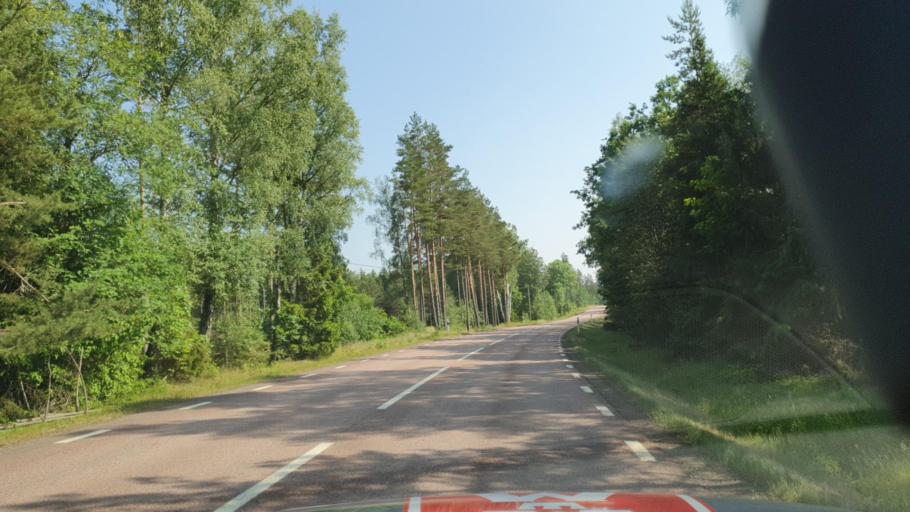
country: SE
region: Kalmar
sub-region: Nybro Kommun
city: Nybro
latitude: 56.8089
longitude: 15.7857
